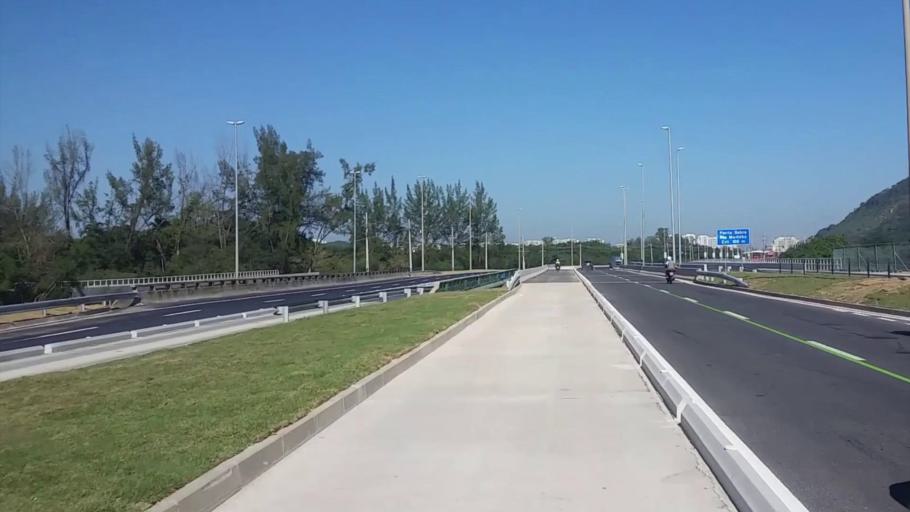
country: BR
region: Rio de Janeiro
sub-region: Nilopolis
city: Nilopolis
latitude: -22.9788
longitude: -43.4079
